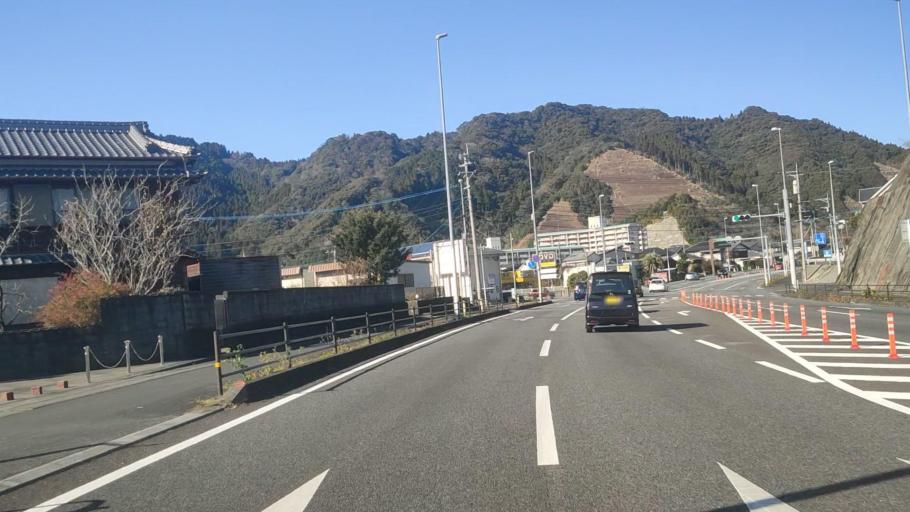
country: JP
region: Oita
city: Saiki
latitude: 32.9621
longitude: 131.8626
